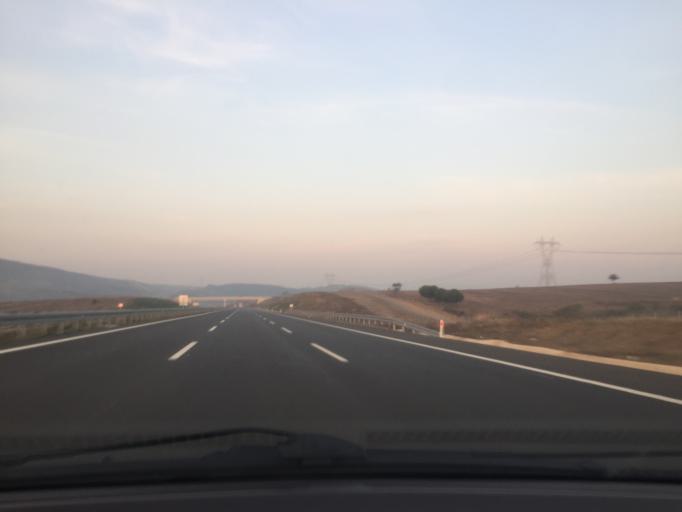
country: TR
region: Bursa
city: Mahmudiye
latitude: 40.2745
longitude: 28.5844
